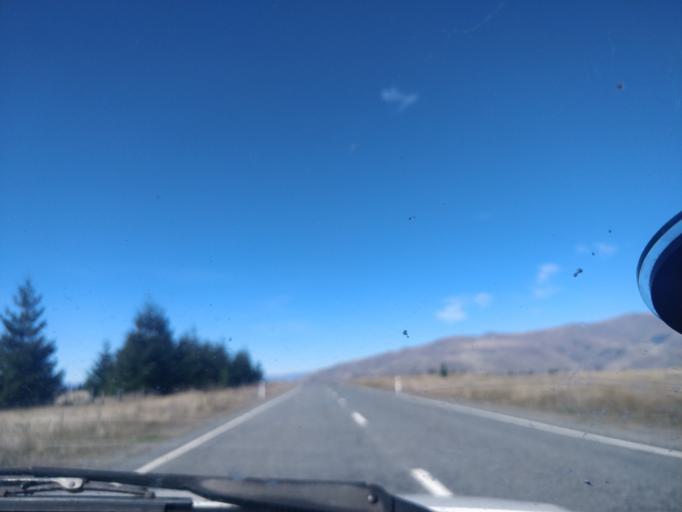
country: NZ
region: Otago
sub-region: Queenstown-Lakes District
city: Wanaka
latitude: -44.2697
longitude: 170.0431
